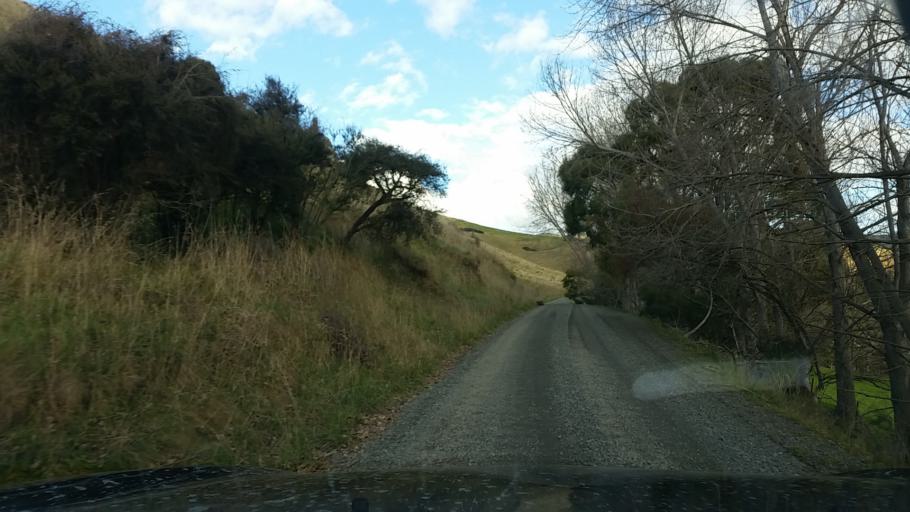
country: NZ
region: Marlborough
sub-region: Marlborough District
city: Blenheim
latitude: -41.7667
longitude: 173.8577
